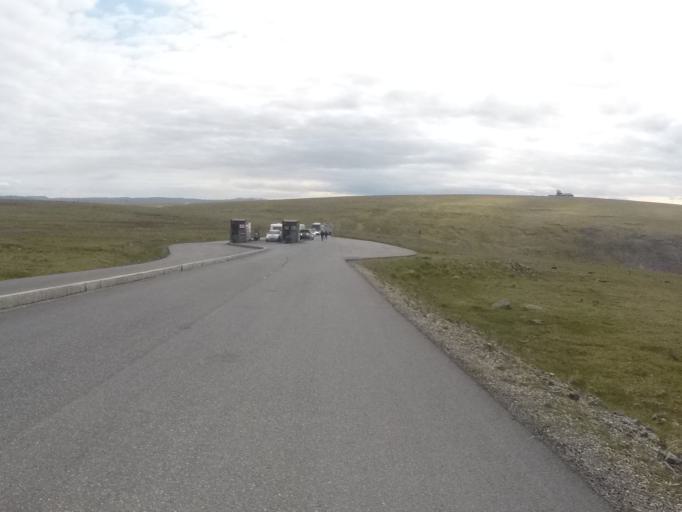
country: NO
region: Finnmark Fylke
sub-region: Nordkapp
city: Honningsvag
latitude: 71.1676
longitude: 25.7812
